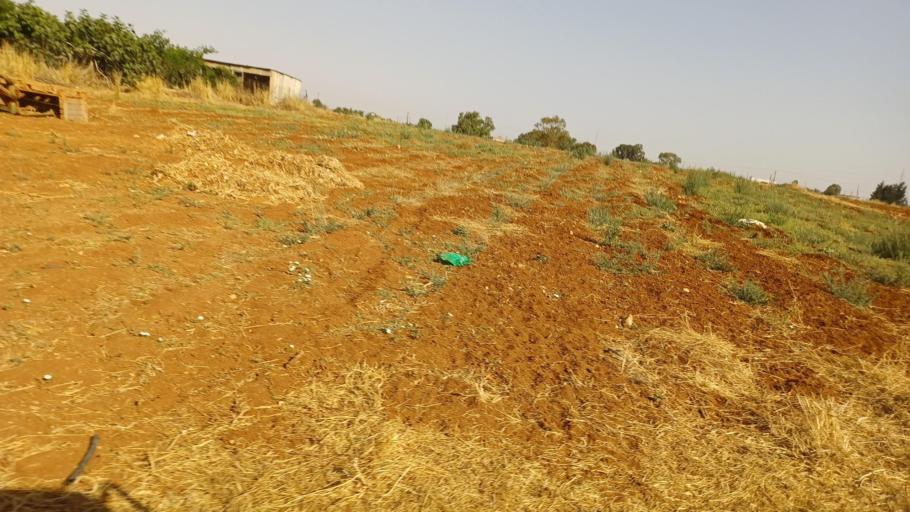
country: CY
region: Ammochostos
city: Liopetri
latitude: 34.9912
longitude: 33.8817
